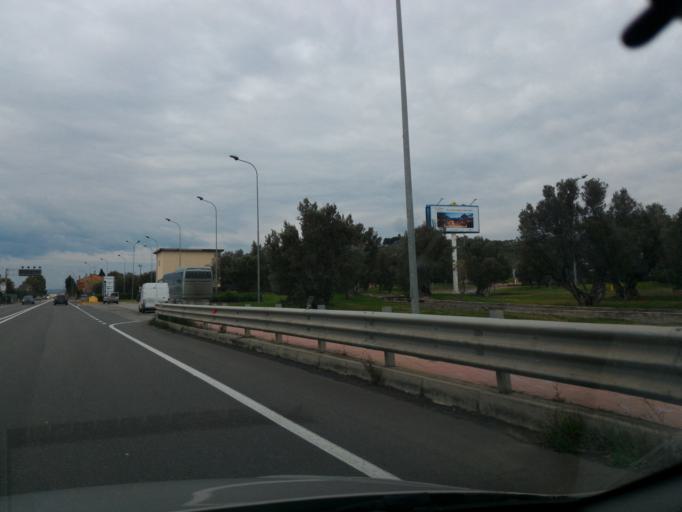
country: IT
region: Calabria
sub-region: Provincia di Catanzaro
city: Barone
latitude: 38.8420
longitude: 16.6481
